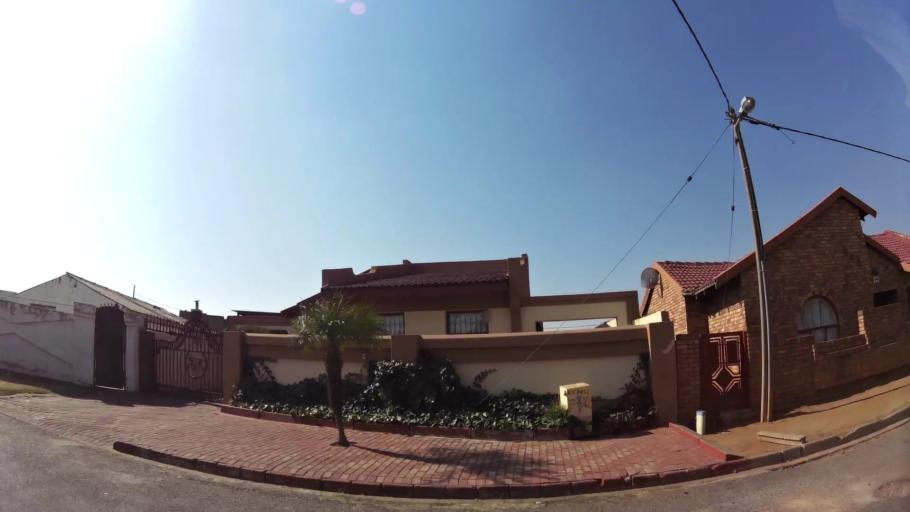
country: ZA
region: Gauteng
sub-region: Ekurhuleni Metropolitan Municipality
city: Boksburg
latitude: -26.2195
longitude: 28.2934
